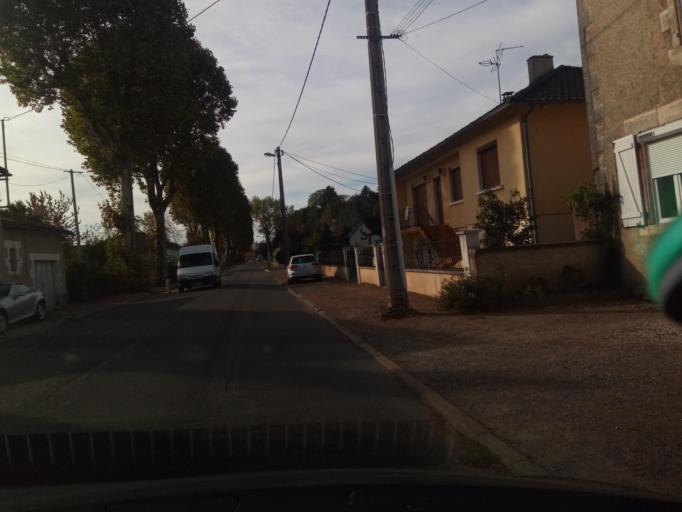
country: FR
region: Poitou-Charentes
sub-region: Departement de la Vienne
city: Montmorillon
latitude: 46.4196
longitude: 0.8768
